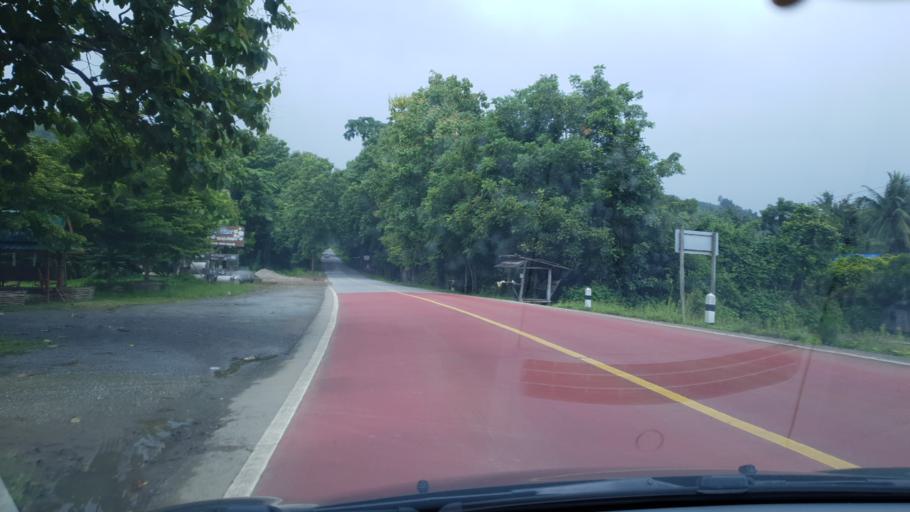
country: TH
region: Mae Hong Son
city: Mae La Noi
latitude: 18.3096
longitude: 97.9116
